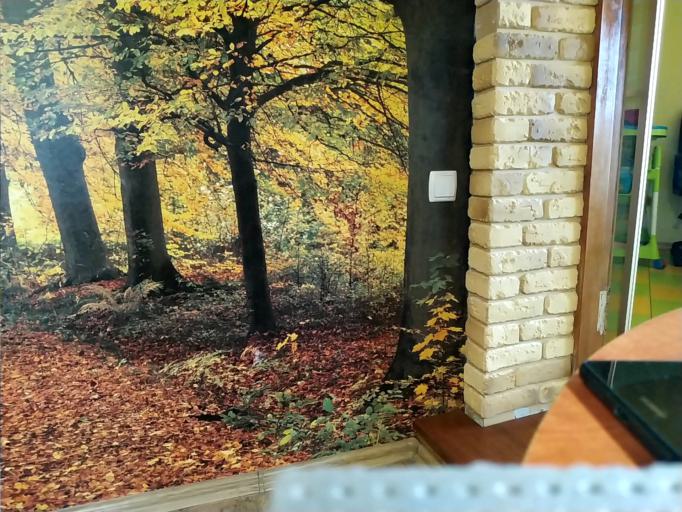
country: RU
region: Kaluga
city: Iznoski
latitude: 54.8599
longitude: 35.4293
